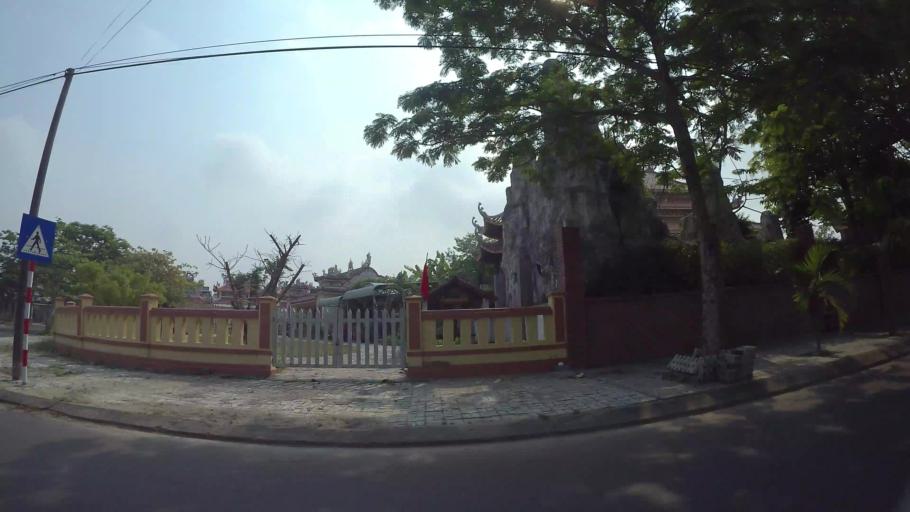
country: VN
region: Da Nang
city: Cam Le
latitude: 16.0028
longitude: 108.2148
